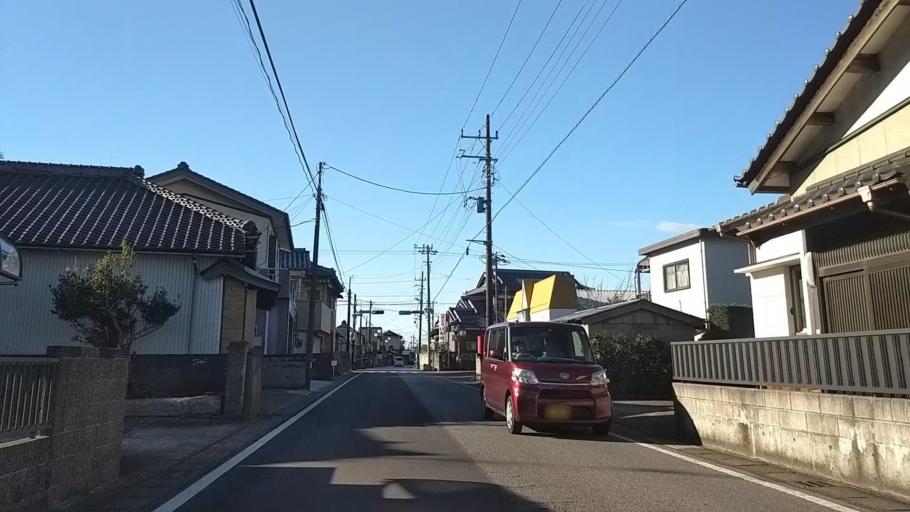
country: JP
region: Chiba
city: Futtsu
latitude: 35.2838
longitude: 139.8572
